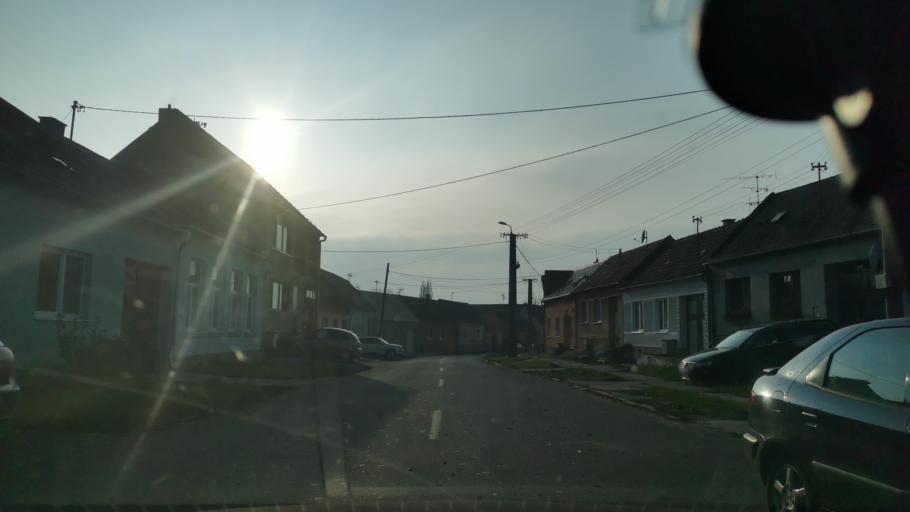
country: SK
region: Trnavsky
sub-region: Okres Senica
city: Senica
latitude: 48.7721
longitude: 17.3166
